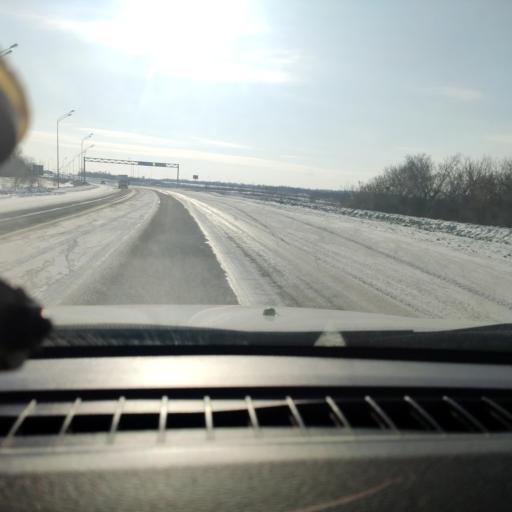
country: RU
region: Samara
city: Smyshlyayevka
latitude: 53.1536
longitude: 50.3973
